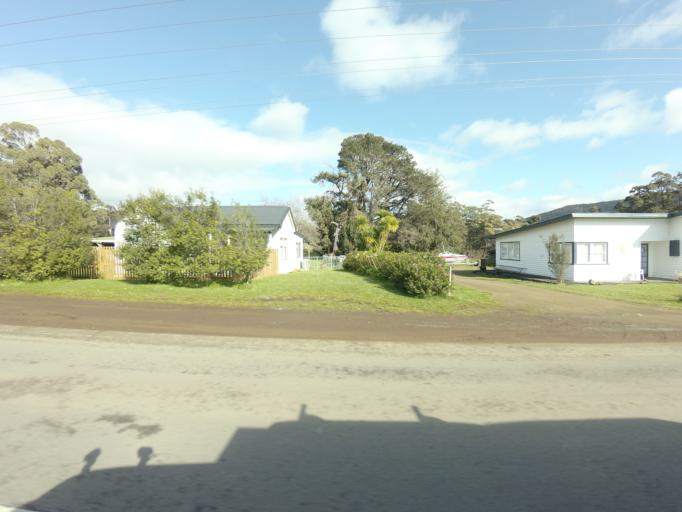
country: AU
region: Tasmania
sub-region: Huon Valley
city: Geeveston
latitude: -43.3348
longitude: 146.9712
